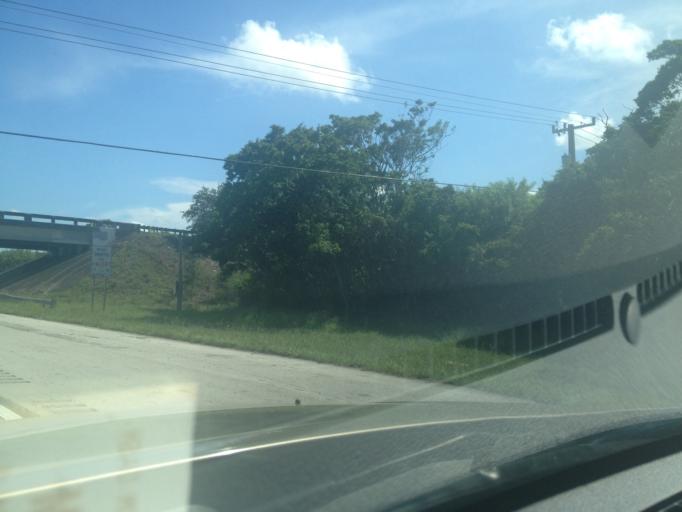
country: US
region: Florida
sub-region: Broward County
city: Deerfield Beach
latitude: 26.3326
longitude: -80.1175
